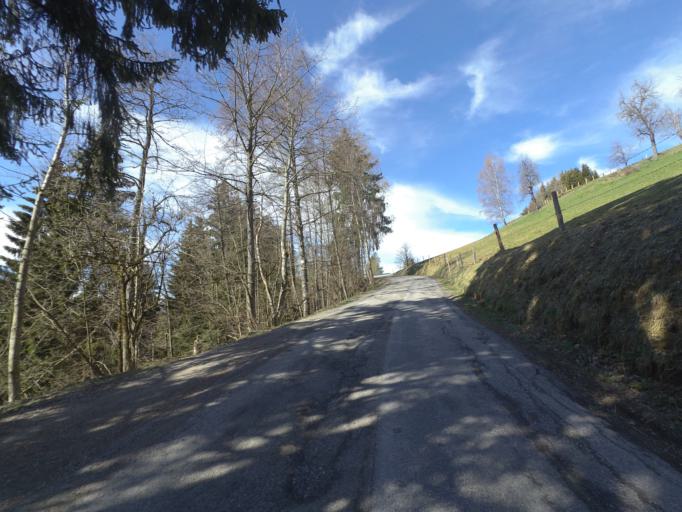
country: AT
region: Salzburg
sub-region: Politischer Bezirk Sankt Johann im Pongau
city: Sankt Veit im Pongau
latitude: 47.3362
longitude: 13.1341
